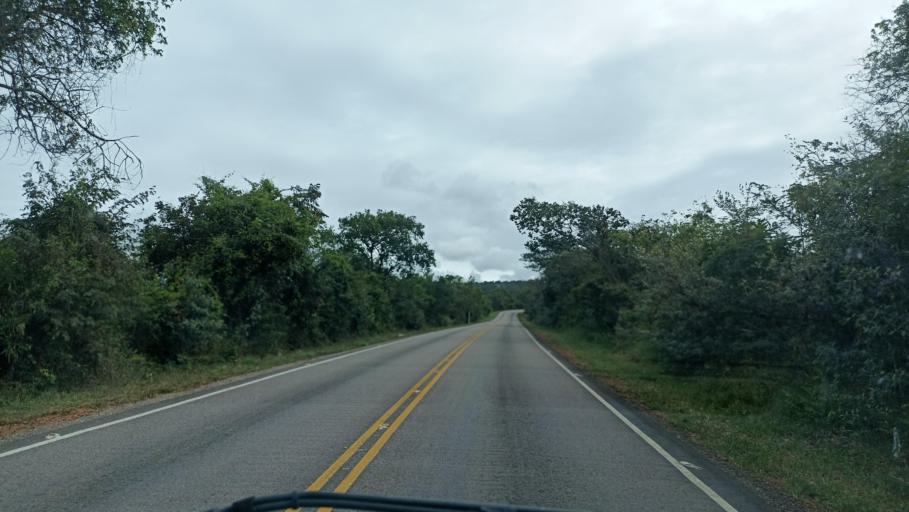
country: BR
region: Bahia
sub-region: Andarai
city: Vera Cruz
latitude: -12.9296
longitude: -41.2356
